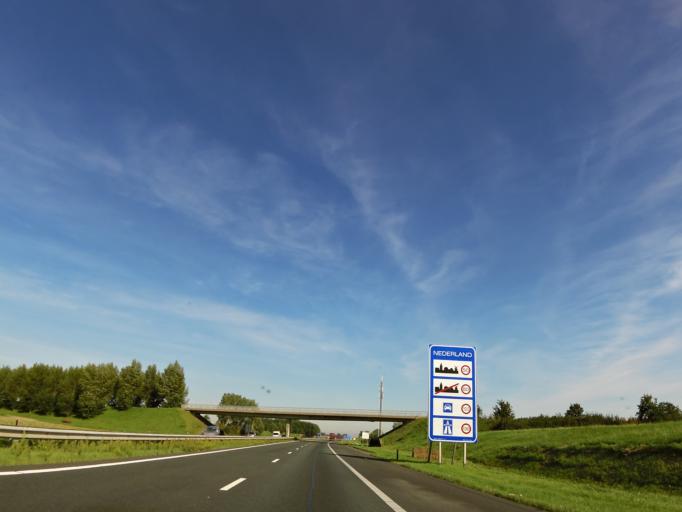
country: NL
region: North Brabant
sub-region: Gemeente Woensdrecht
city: Woensdrecht
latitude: 51.3925
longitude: 4.2917
